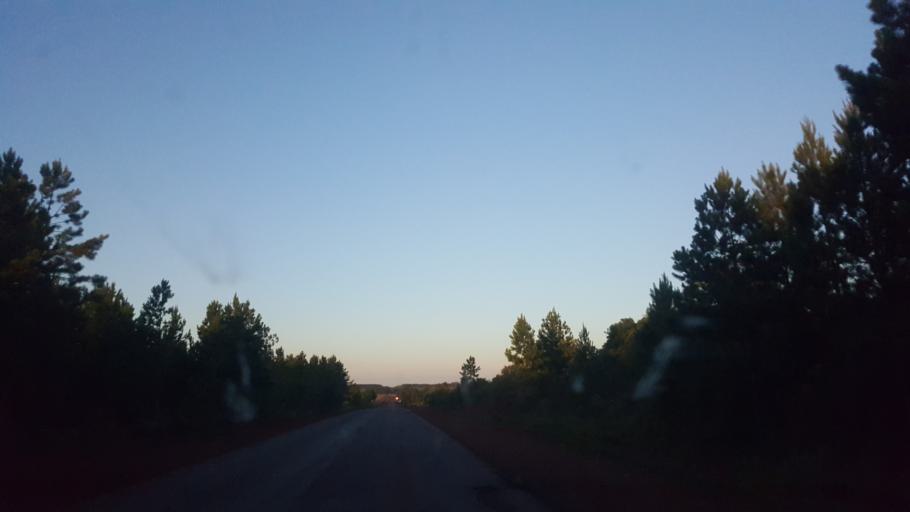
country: AR
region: Corrientes
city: Santo Tome
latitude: -28.3944
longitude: -55.9710
